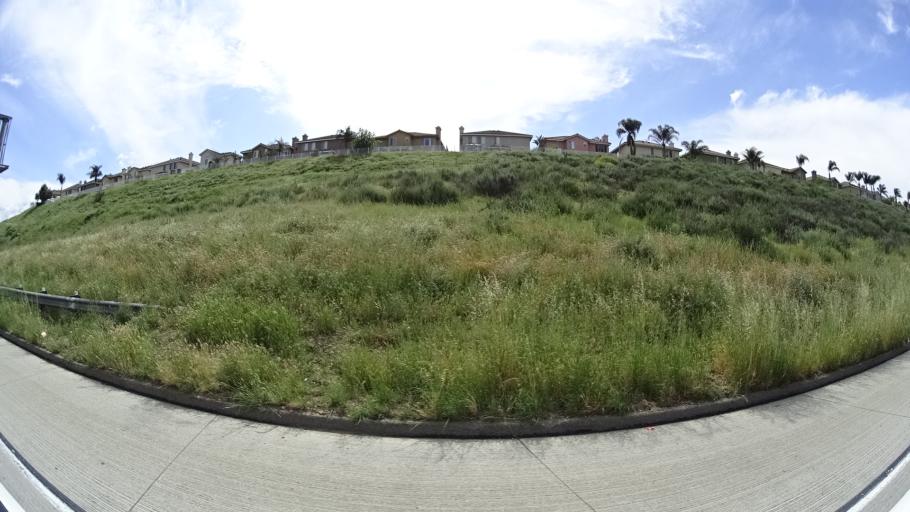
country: US
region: California
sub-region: San Bernardino County
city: Los Serranos
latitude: 33.9406
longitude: -117.6687
